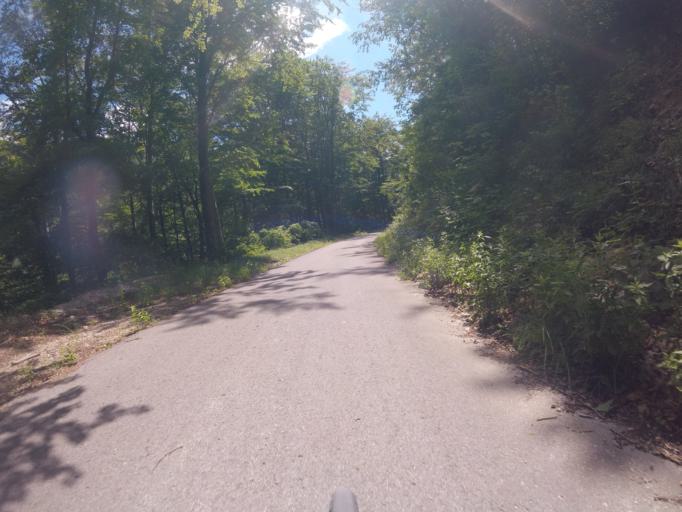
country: SI
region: Kostanjevica na Krki
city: Kostanjevica na Krki
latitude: 45.7701
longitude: 15.4117
